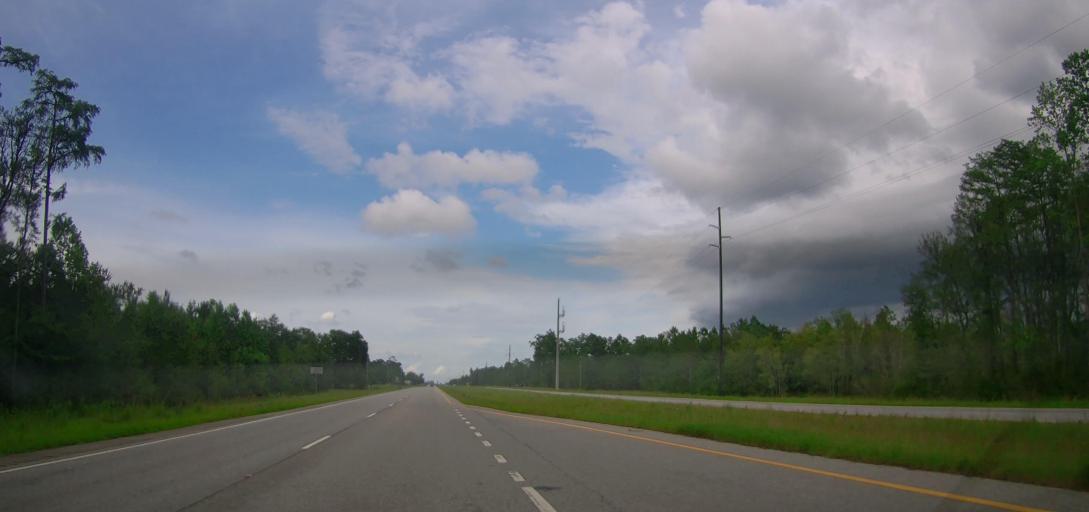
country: US
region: Georgia
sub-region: Pierce County
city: Blackshear
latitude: 31.4194
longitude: -82.1015
